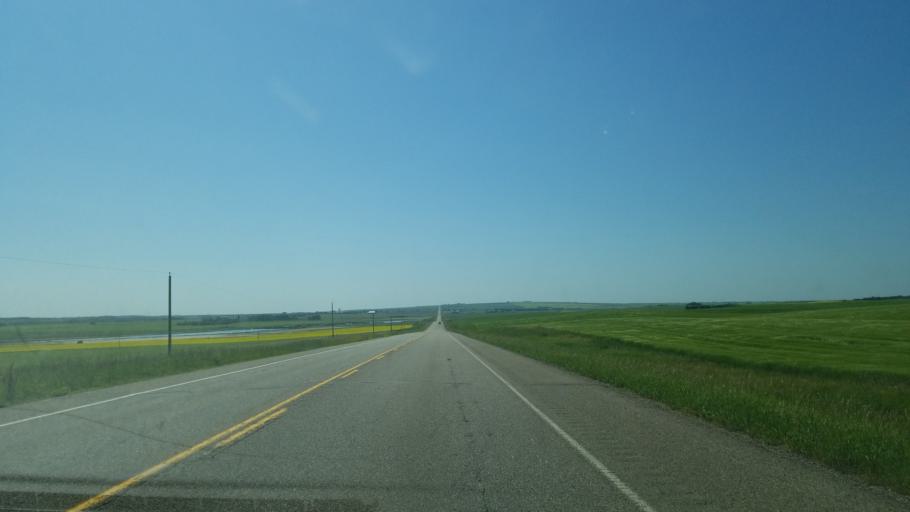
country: CA
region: Saskatchewan
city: Macklin
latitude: 52.3613
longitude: -110.0457
